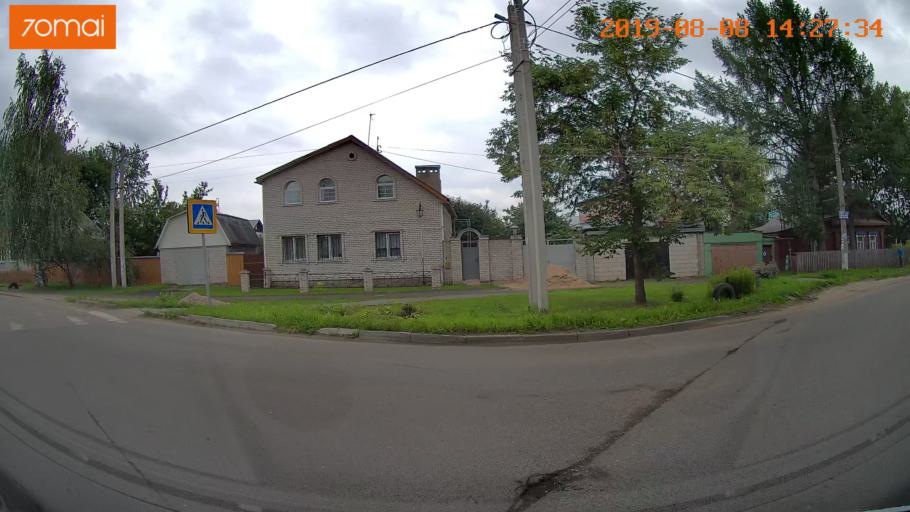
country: RU
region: Ivanovo
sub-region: Gorod Ivanovo
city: Ivanovo
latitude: 56.9965
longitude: 40.9411
